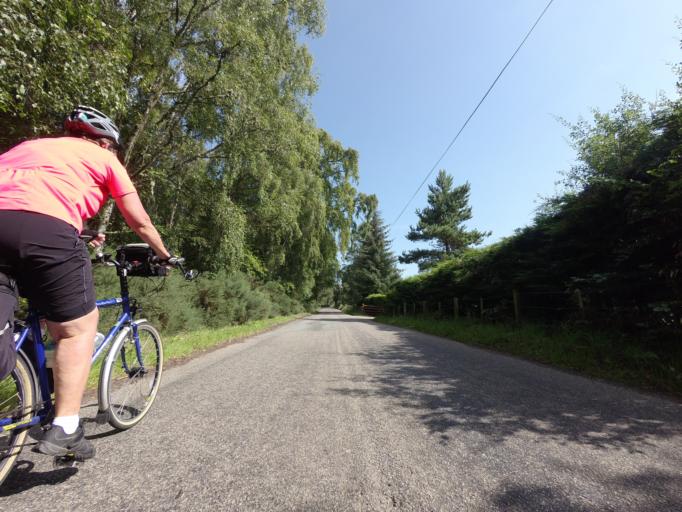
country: GB
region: Scotland
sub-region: Highland
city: Invergordon
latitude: 57.7305
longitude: -4.1926
